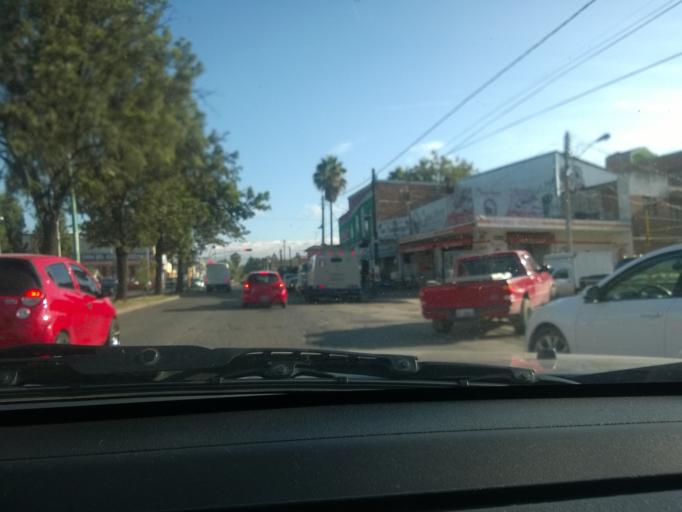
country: MX
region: Guanajuato
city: Leon
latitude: 21.1330
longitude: -101.6650
